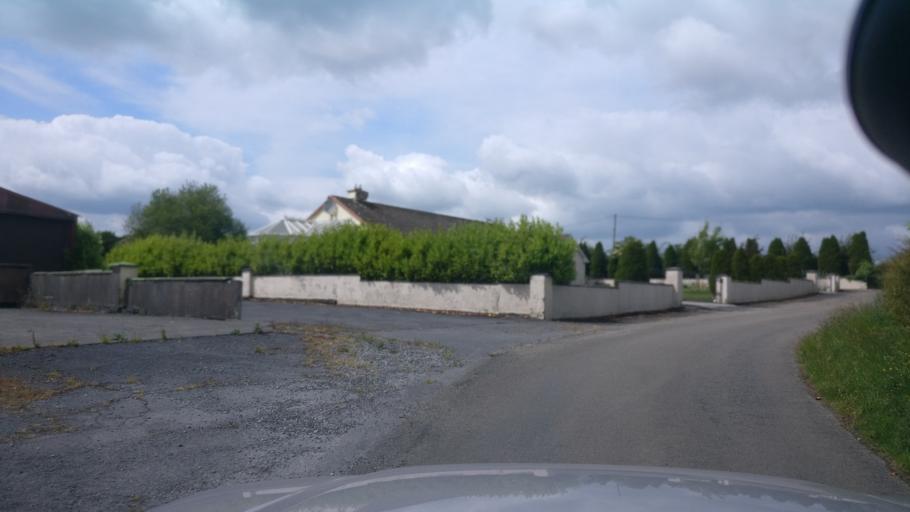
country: IE
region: Connaught
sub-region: County Galway
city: Ballinasloe
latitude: 53.2882
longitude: -8.3173
